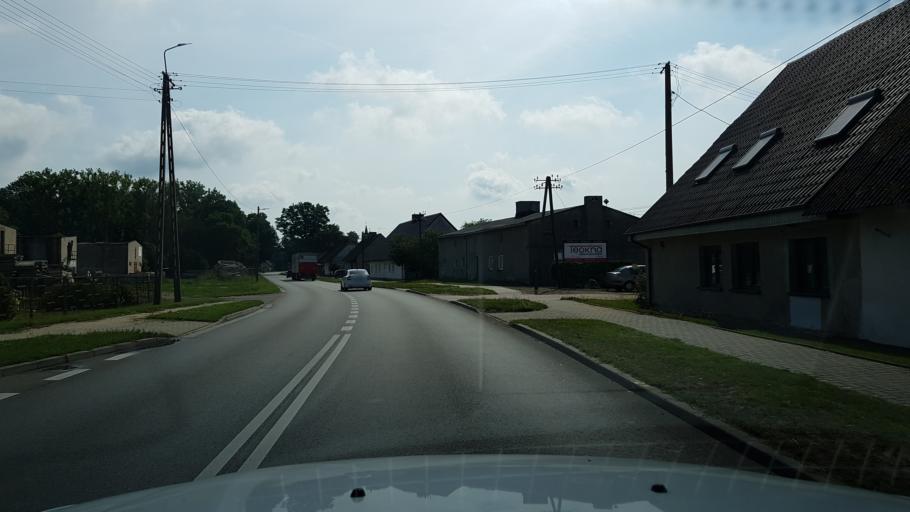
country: PL
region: West Pomeranian Voivodeship
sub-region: Powiat walecki
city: Walcz
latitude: 53.3151
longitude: 16.3421
